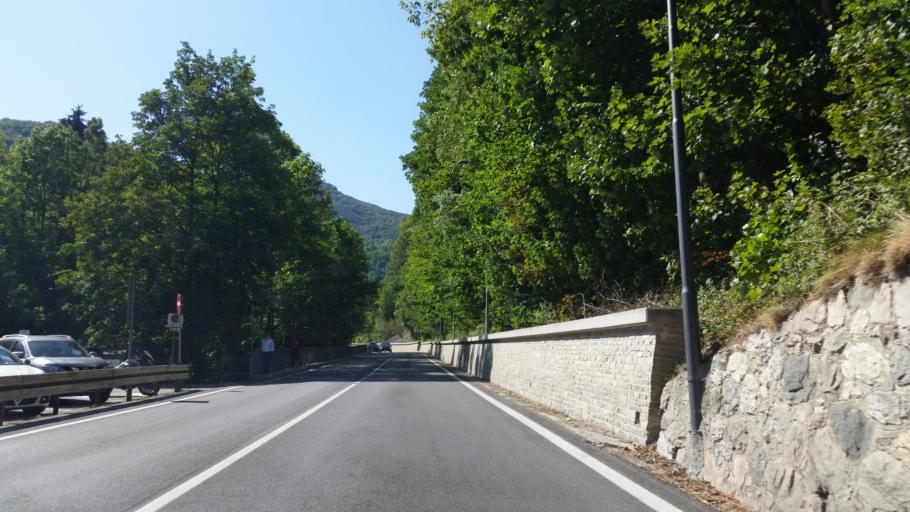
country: IT
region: Piedmont
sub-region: Provincia di Cuneo
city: Limone Piemonte
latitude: 44.2017
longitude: 7.5744
